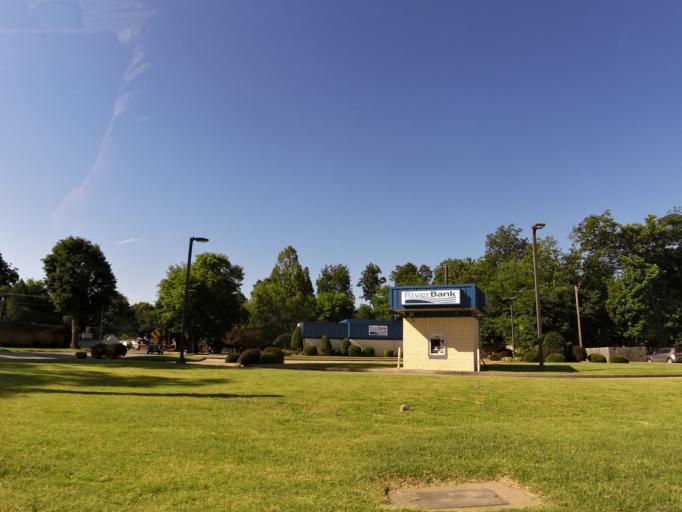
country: US
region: Arkansas
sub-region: Clay County
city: Corning
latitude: 36.4113
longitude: -90.5866
